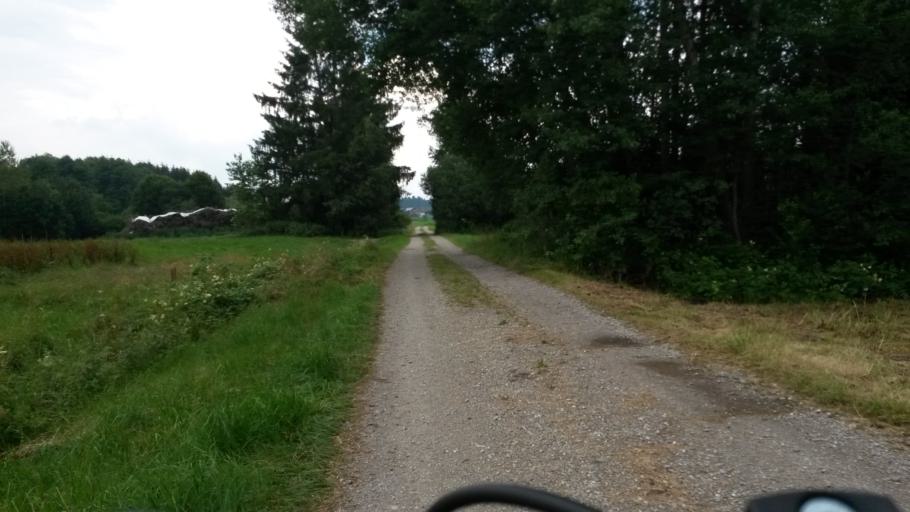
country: DE
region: Bavaria
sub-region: Upper Bavaria
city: Hoslwang
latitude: 47.9383
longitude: 12.3288
